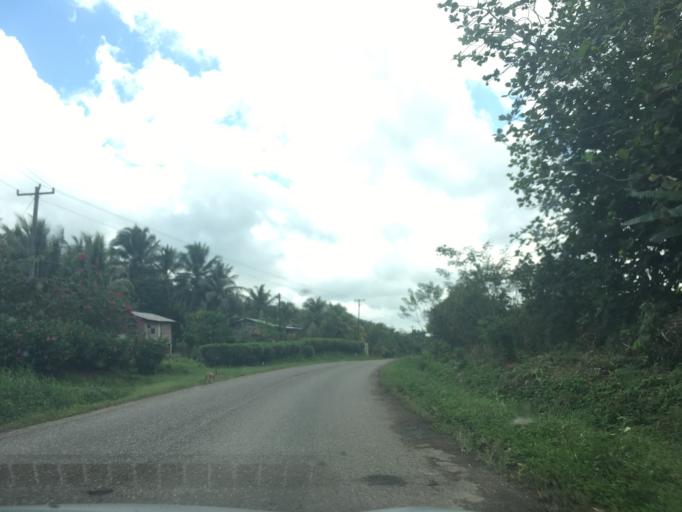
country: BZ
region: Stann Creek
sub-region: Dangriga
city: Dangriga
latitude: 17.0005
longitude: -88.4214
